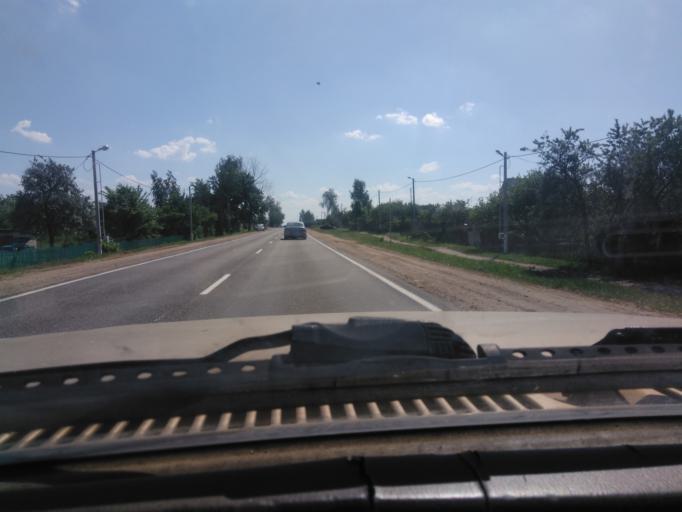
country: BY
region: Mogilev
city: Palykavichy Pyershyya
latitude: 54.0272
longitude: 30.3230
